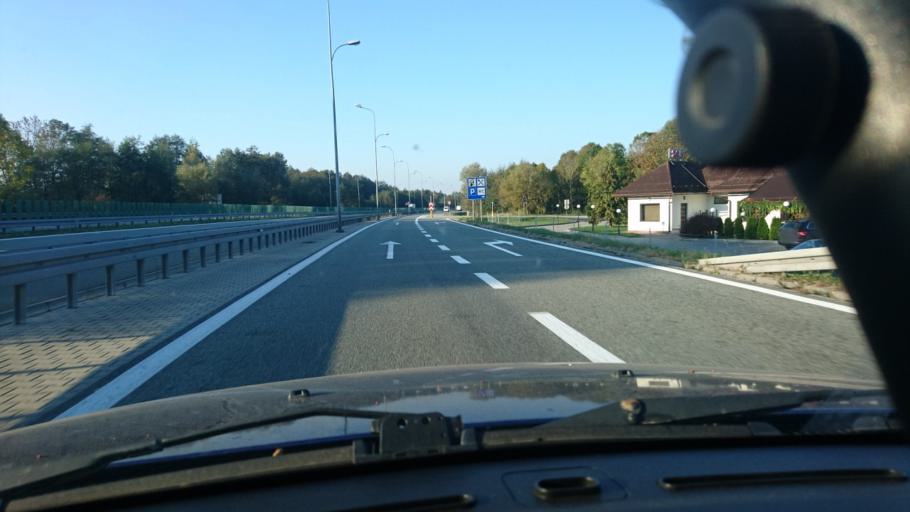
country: PL
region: Silesian Voivodeship
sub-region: Powiat cieszynski
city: Gorki Wielkie
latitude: 49.7895
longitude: 18.8245
